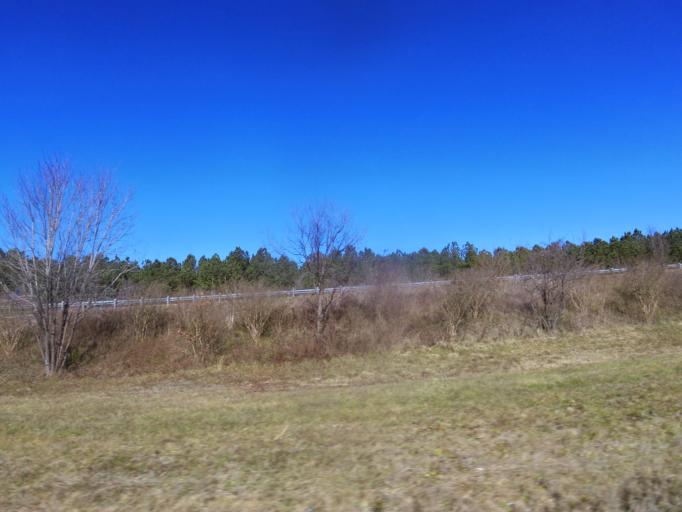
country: US
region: Virginia
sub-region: Isle of Wight County
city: Smithfield
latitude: 36.9713
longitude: -76.6334
